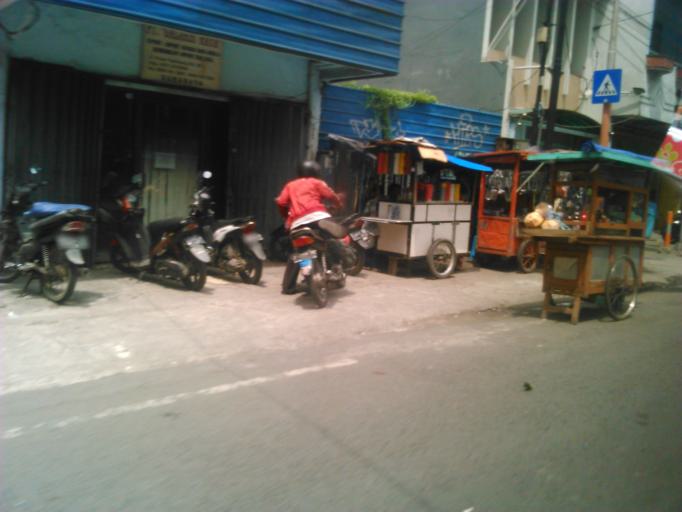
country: ID
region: East Java
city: Gubengairlangga
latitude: -7.2708
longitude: 112.7283
